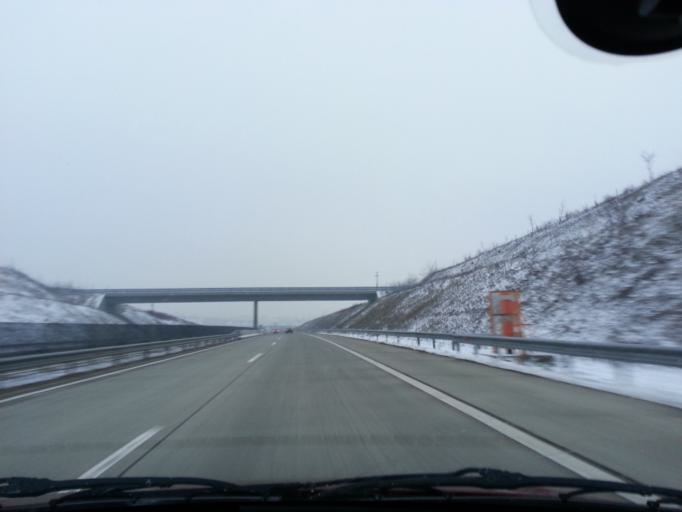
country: HU
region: Pest
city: Nagytarcsa
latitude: 47.5361
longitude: 19.3055
